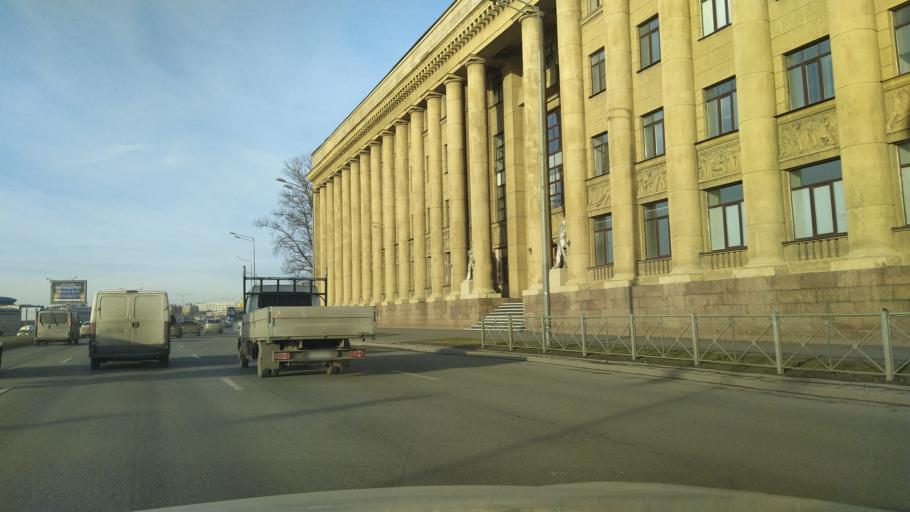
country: RU
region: St.-Petersburg
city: Centralniy
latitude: 59.9275
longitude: 30.4001
